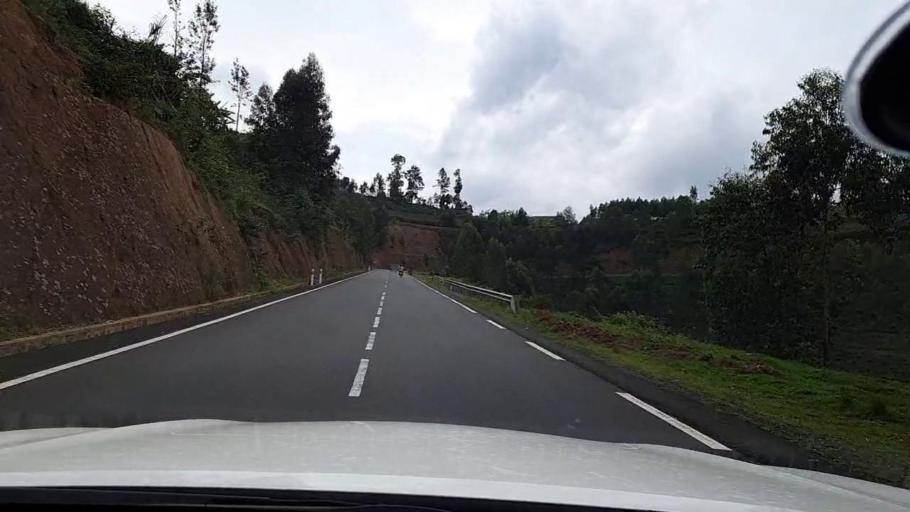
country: RW
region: Western Province
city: Kibuye
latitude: -2.1727
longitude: 29.2907
